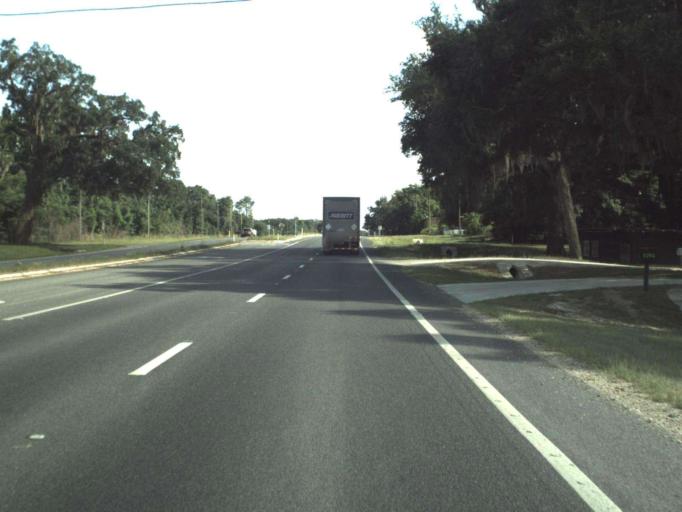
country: US
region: Florida
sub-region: Sumter County
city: Wildwood
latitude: 28.8919
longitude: -82.0371
